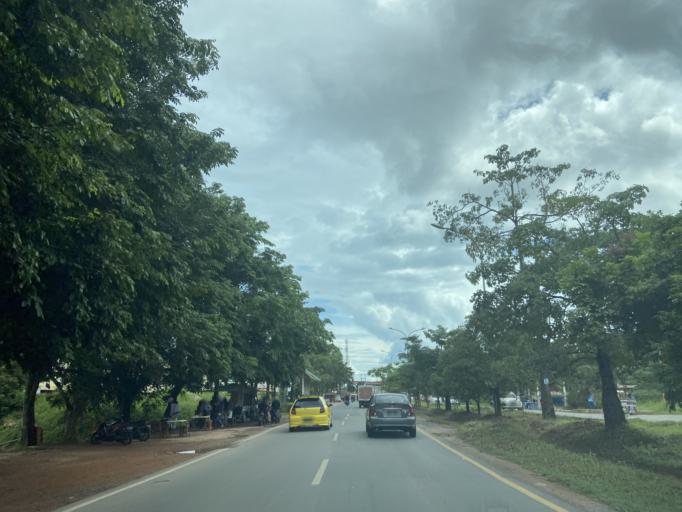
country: SG
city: Singapore
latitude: 1.0411
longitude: 103.9881
